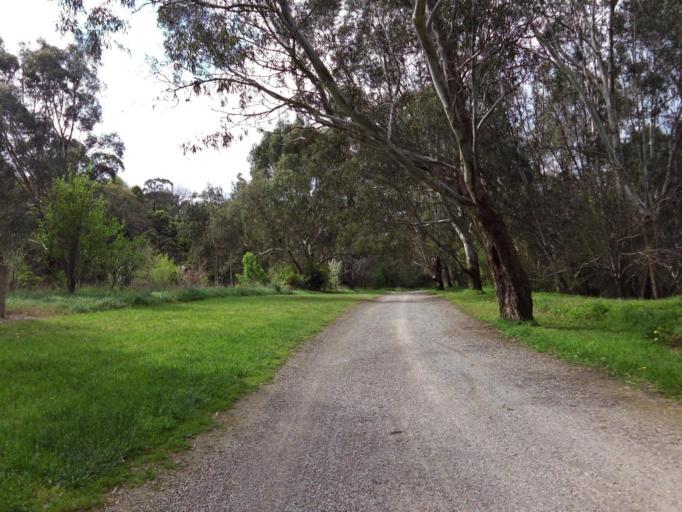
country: AU
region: Victoria
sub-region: Manningham
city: Bulleen
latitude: -37.7726
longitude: 145.0688
